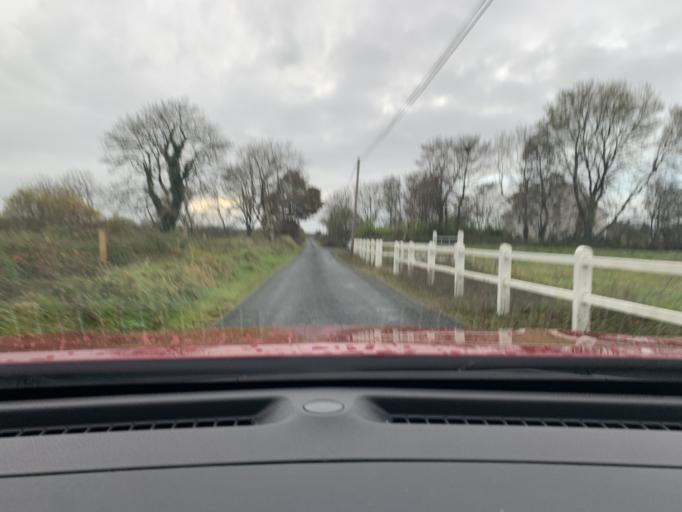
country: IE
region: Connaught
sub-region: Roscommon
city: Ballaghaderreen
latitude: 53.9675
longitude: -8.5793
